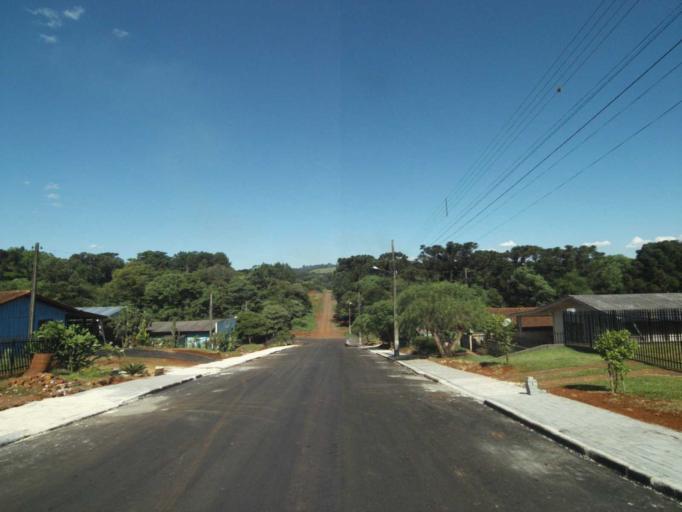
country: BR
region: Parana
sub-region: Laranjeiras Do Sul
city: Laranjeiras do Sul
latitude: -25.3839
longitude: -52.2029
